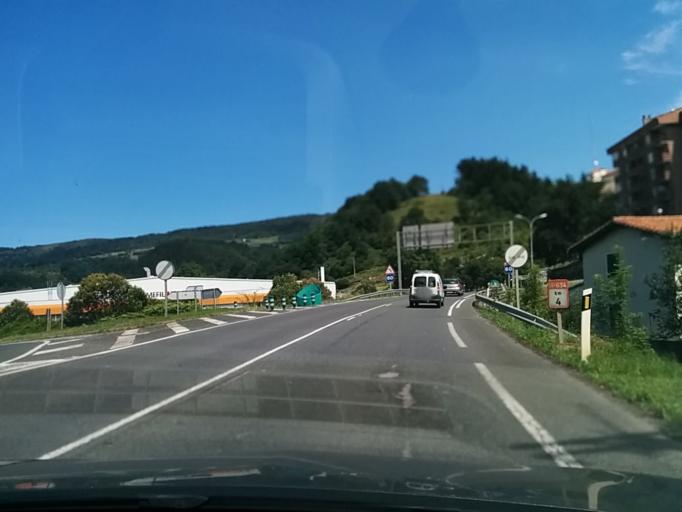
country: ES
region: Basque Country
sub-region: Provincia de Guipuzcoa
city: Usurbil
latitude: 43.2717
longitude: -2.0538
